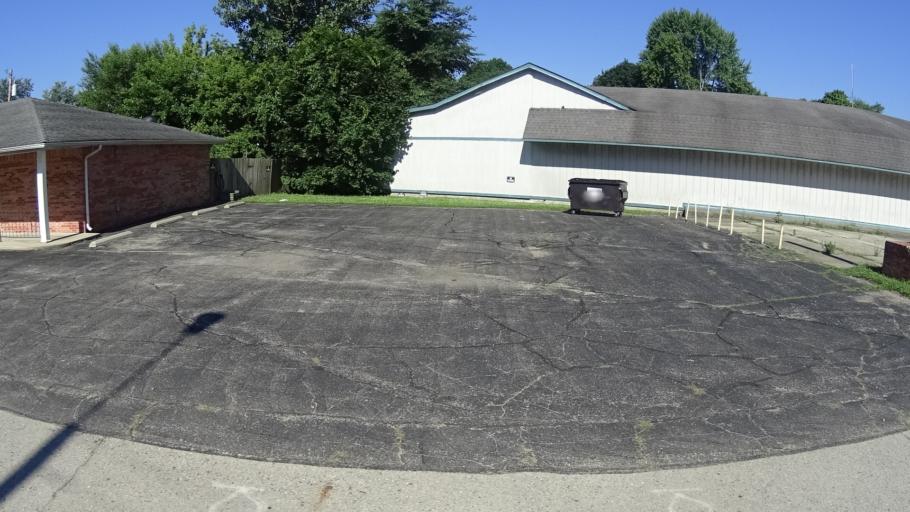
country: US
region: Indiana
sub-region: Madison County
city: Pendleton
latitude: 40.0008
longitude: -85.7457
